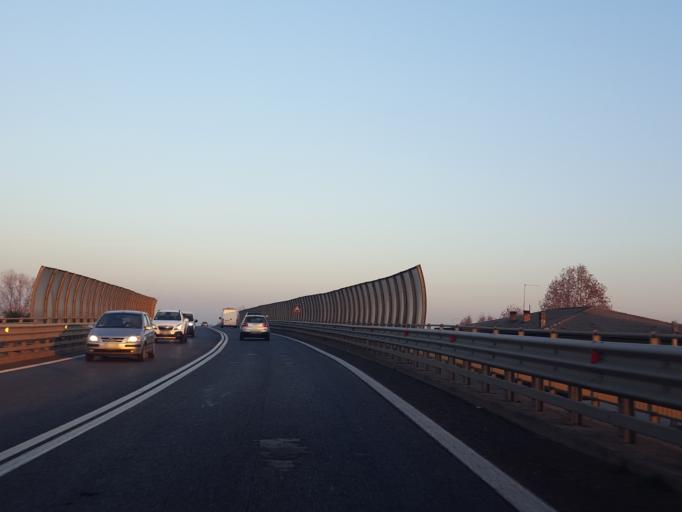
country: IT
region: Veneto
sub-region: Provincia di Vicenza
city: Lisiera
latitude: 45.5823
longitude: 11.6134
